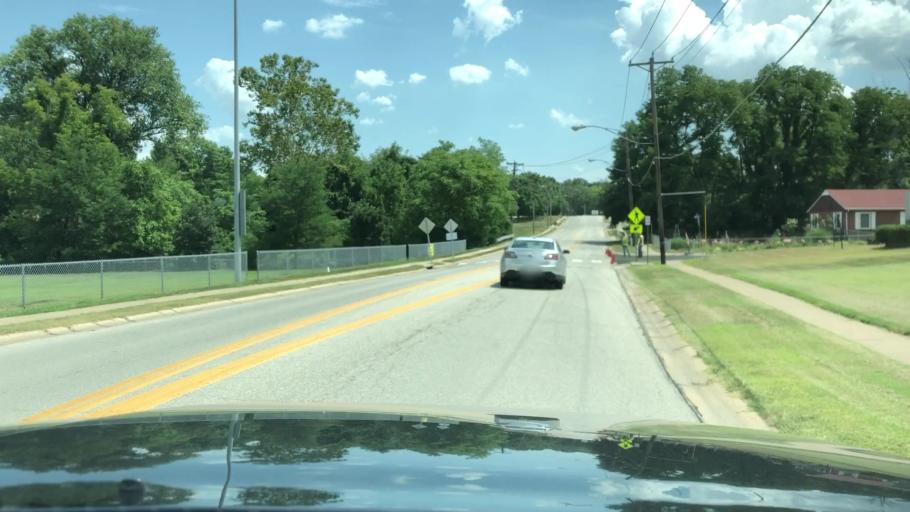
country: US
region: Missouri
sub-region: Saint Charles County
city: Saint Charles
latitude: 38.7976
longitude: -90.5258
